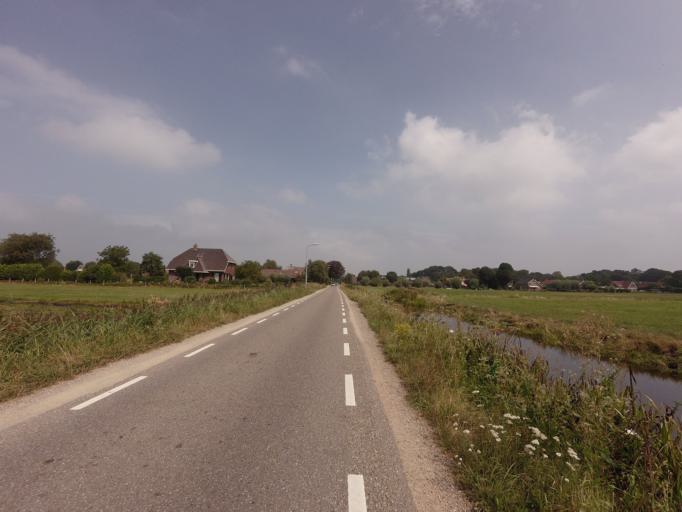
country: NL
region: North Holland
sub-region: Gemeente Wijdemeren
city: Kortenhoef
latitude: 52.2482
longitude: 5.1146
